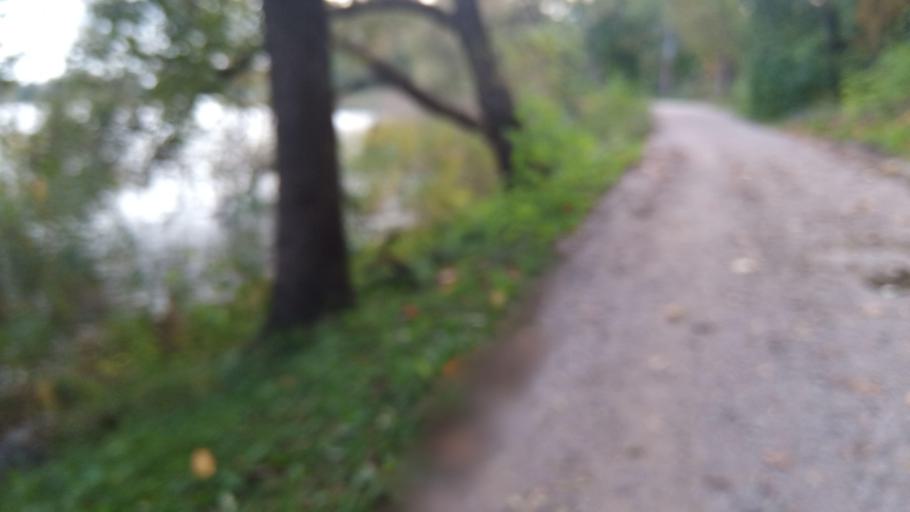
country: LT
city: Trakai
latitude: 54.6356
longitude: 24.9401
